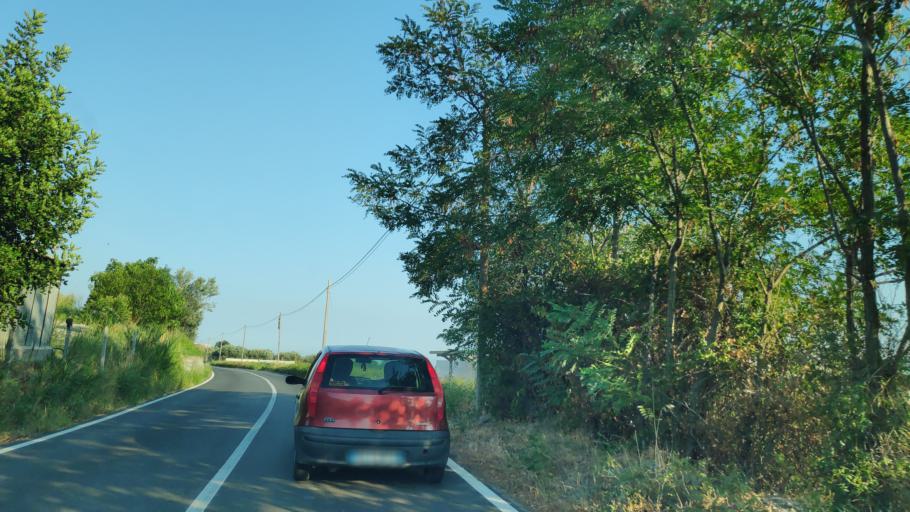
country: IT
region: Calabria
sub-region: Provincia di Reggio Calabria
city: Caulonia Marina
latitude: 38.3675
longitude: 16.4515
